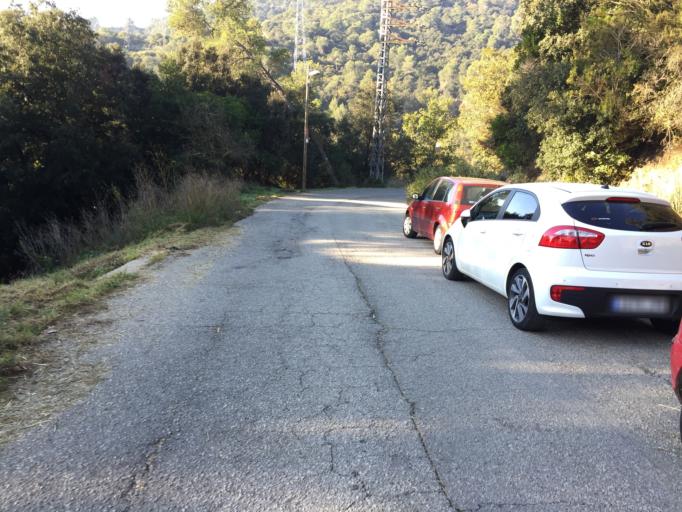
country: ES
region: Catalonia
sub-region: Provincia de Barcelona
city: Sant Just Desvern
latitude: 41.4216
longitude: 2.0971
